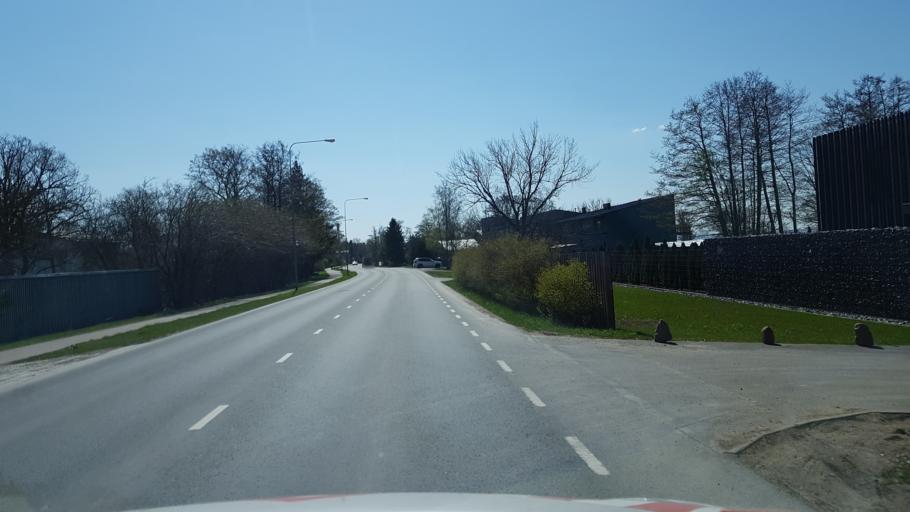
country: EE
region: Harju
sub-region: Viimsi vald
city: Rummu
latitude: 59.5301
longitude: 24.7964
